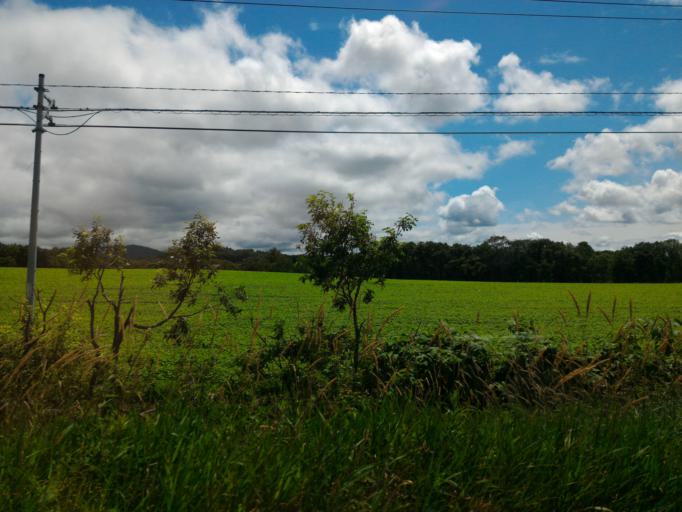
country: JP
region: Hokkaido
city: Nayoro
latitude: 44.6535
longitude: 142.2680
